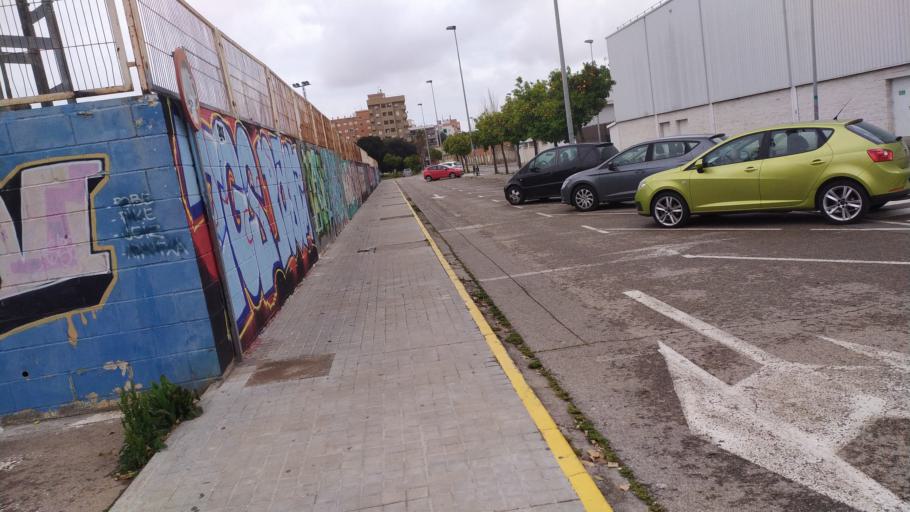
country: ES
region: Valencia
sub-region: Provincia de Valencia
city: Mislata
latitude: 39.4659
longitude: -0.4140
